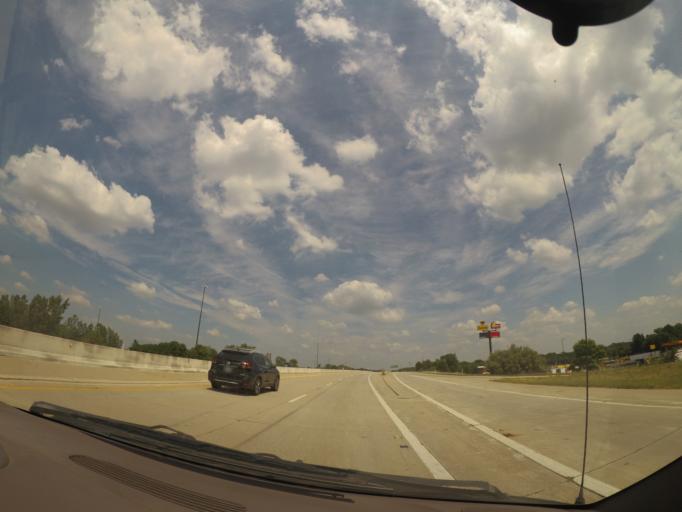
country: US
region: Indiana
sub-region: Elkhart County
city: Dunlap
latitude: 41.6667
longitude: -85.8915
